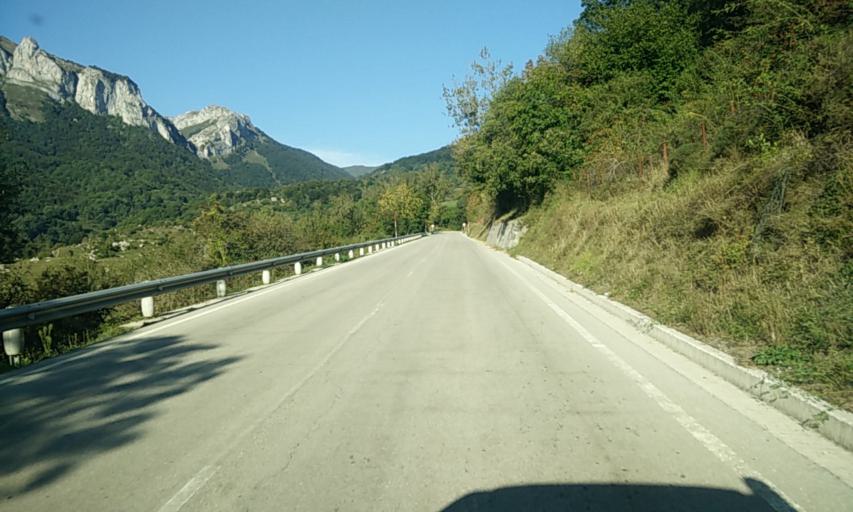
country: ES
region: Cantabria
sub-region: Provincia de Cantabria
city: Camaleno
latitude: 43.1304
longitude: -4.7978
